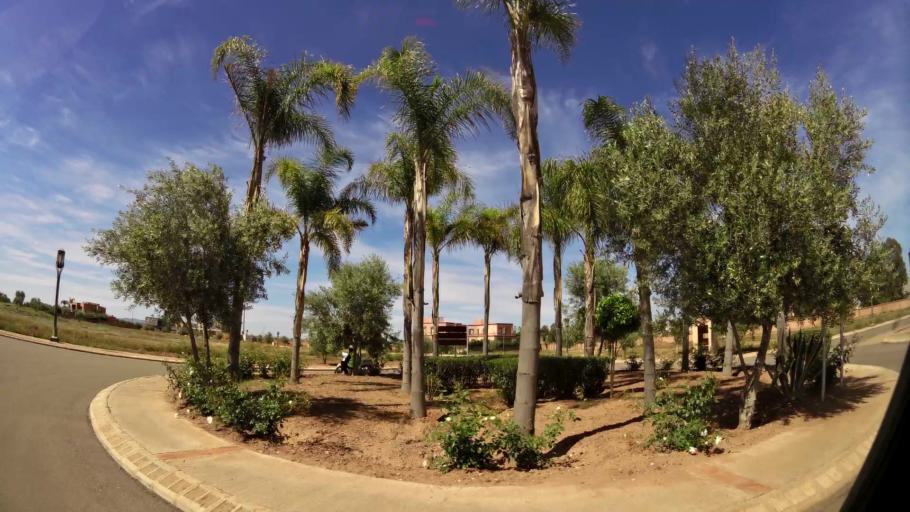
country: MA
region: Marrakech-Tensift-Al Haouz
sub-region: Marrakech
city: Marrakesh
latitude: 31.6194
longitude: -7.9220
